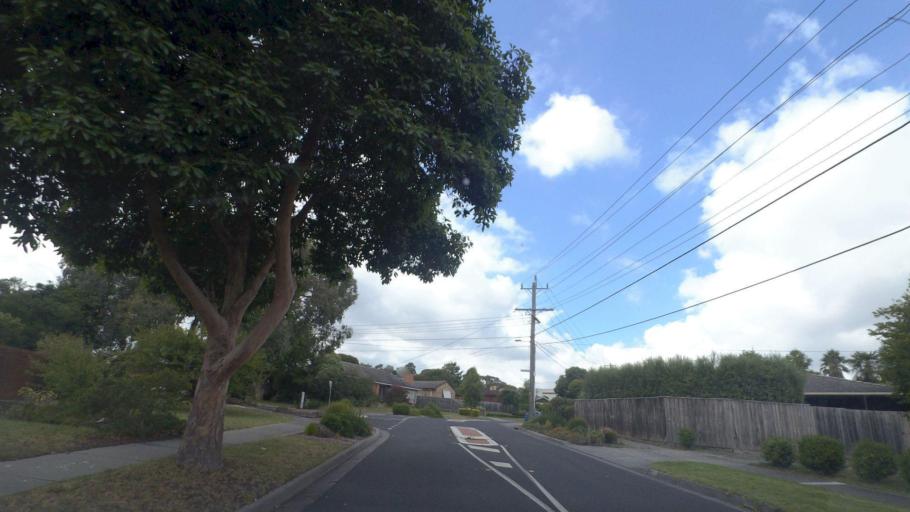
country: AU
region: Victoria
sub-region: Knox
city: Scoresby
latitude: -37.8978
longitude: 145.2264
